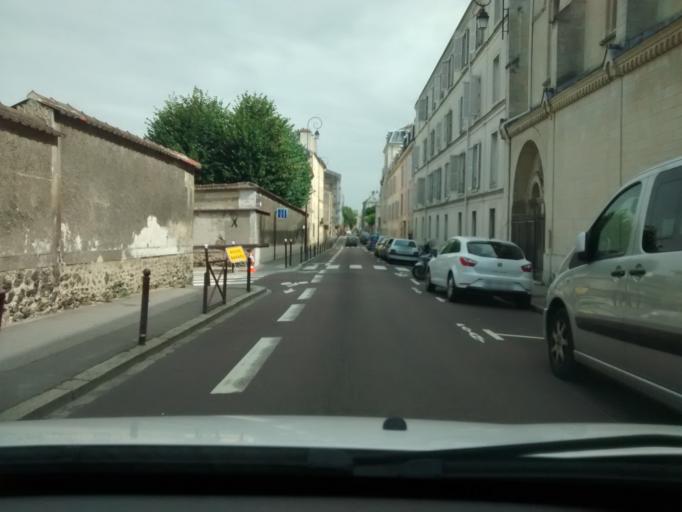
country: FR
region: Ile-de-France
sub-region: Departement des Yvelines
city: Versailles
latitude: 48.7937
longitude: 2.1293
